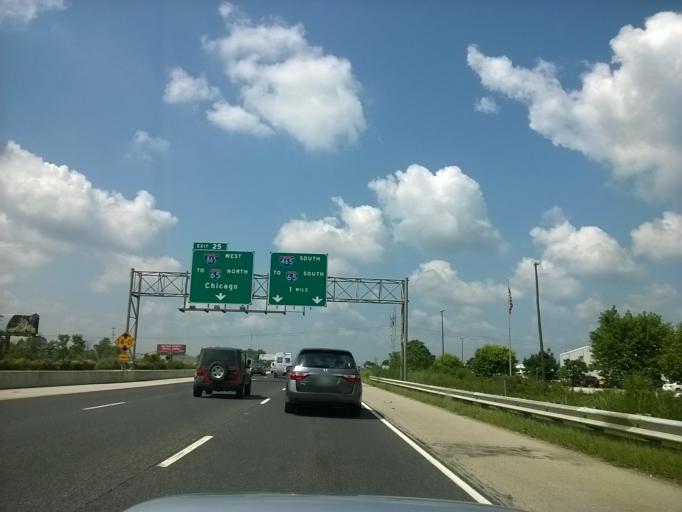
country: US
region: Indiana
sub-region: Boone County
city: Zionsville
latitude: 39.9237
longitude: -86.2380
